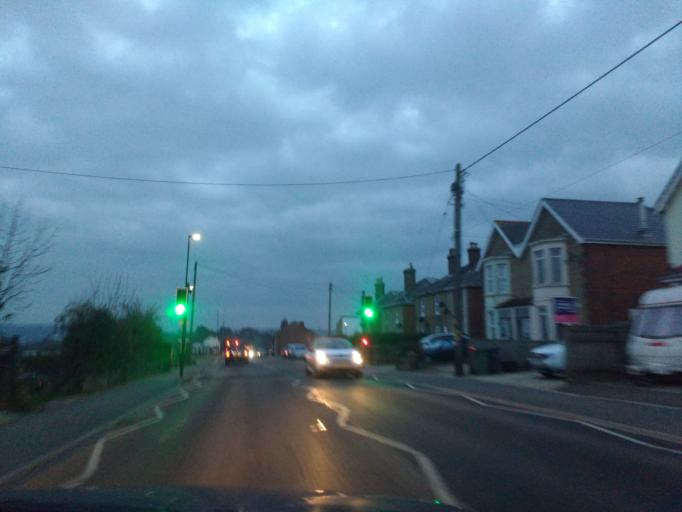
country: GB
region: England
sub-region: Isle of Wight
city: Northwood
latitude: 50.7211
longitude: -1.3045
